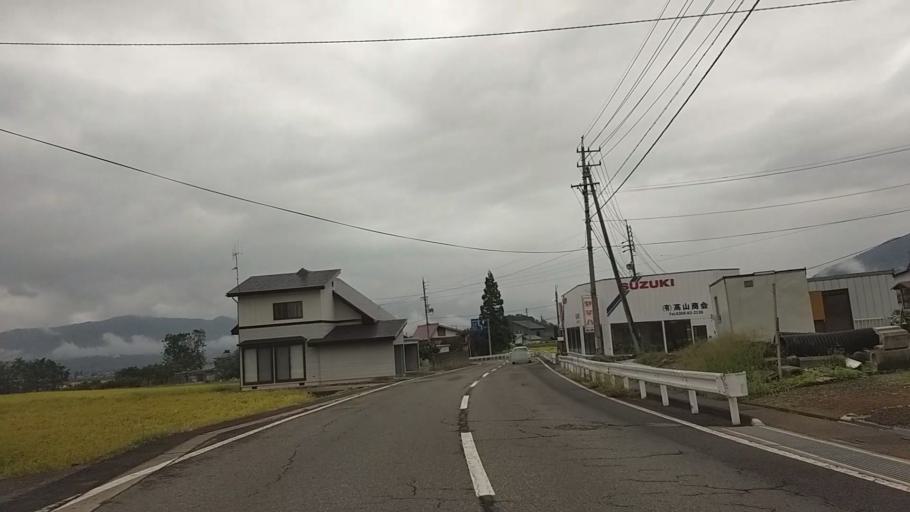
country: JP
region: Nagano
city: Iiyama
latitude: 36.8423
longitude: 138.4060
